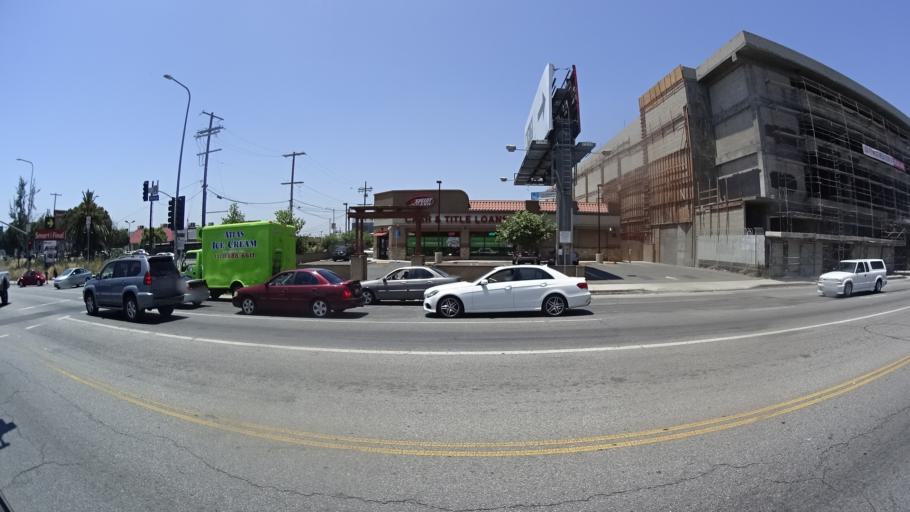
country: US
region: California
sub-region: Los Angeles County
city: Van Nuys
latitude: 34.2137
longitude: -118.4488
